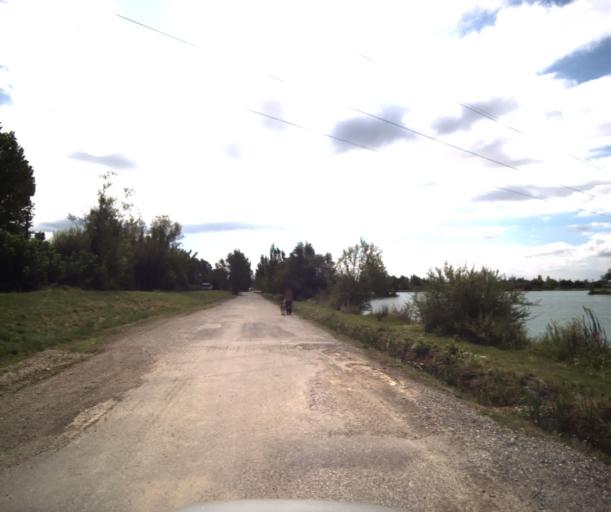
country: FR
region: Midi-Pyrenees
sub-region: Departement de la Haute-Garonne
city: Noe
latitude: 43.3736
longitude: 1.2592
